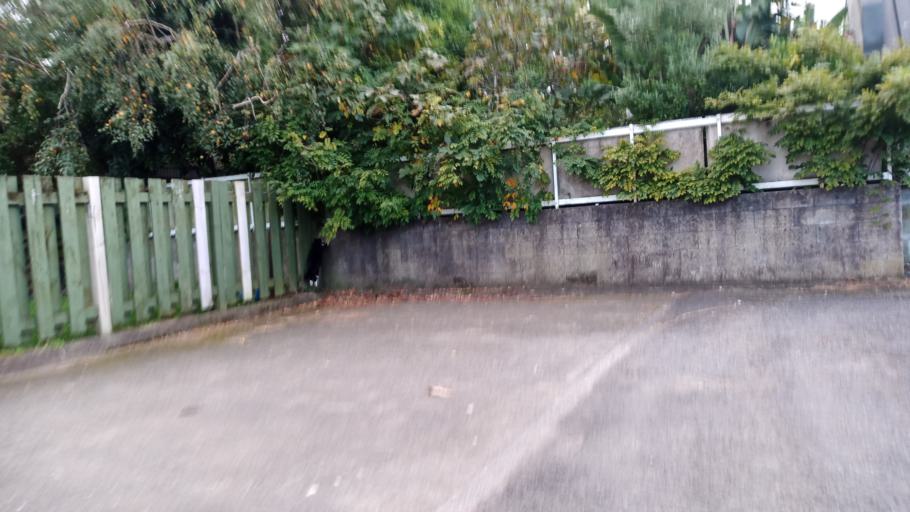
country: NZ
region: Gisborne
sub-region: Gisborne District
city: Gisborne
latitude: -38.6603
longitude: 178.0223
